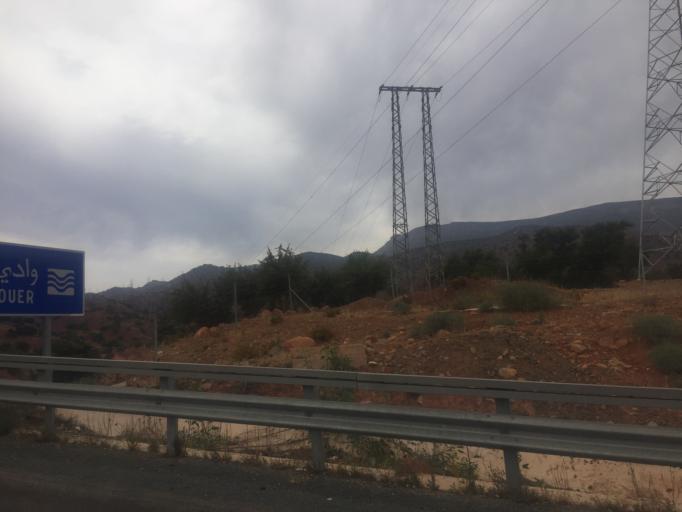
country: MA
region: Souss-Massa-Draa
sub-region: Taroudannt
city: Bigoudine
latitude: 30.6791
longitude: -9.2447
